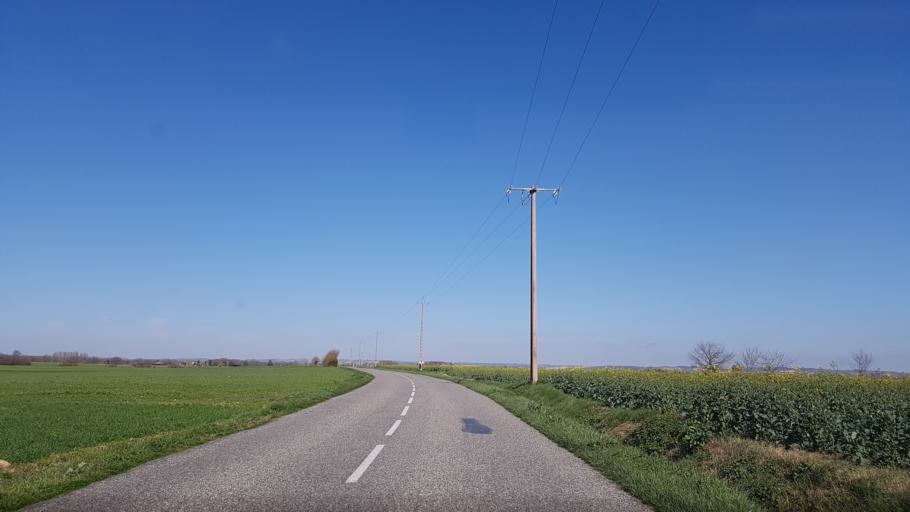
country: FR
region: Languedoc-Roussillon
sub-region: Departement de l'Aude
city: Belpech
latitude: 43.1646
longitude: 1.7102
